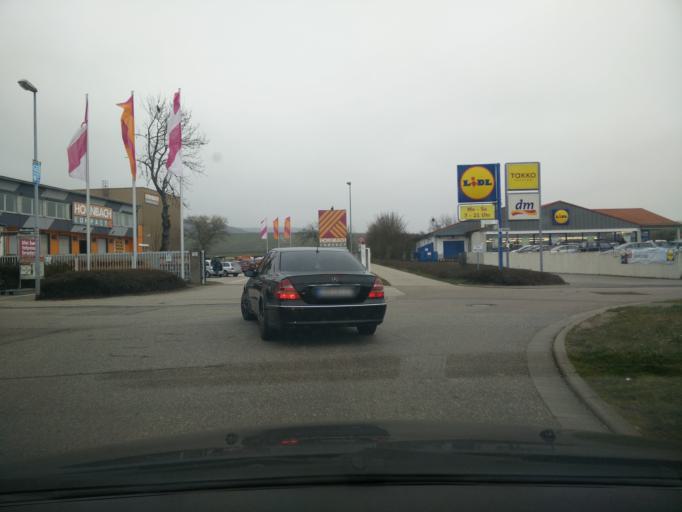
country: DE
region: Rheinland-Pfalz
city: Pleisweiler-Oberhofen
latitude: 49.1074
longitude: 8.0109
